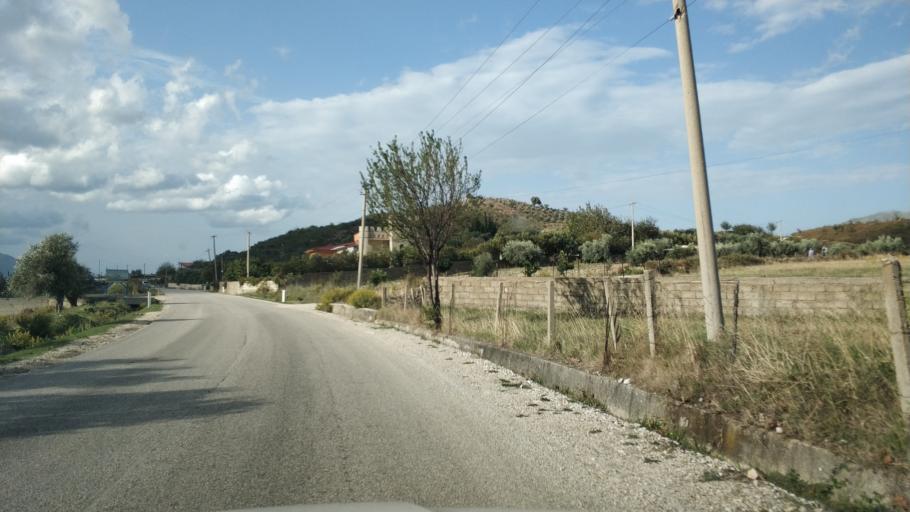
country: AL
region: Vlore
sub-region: Rrethi i Vlores
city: Orikum
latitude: 40.2956
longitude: 19.4903
